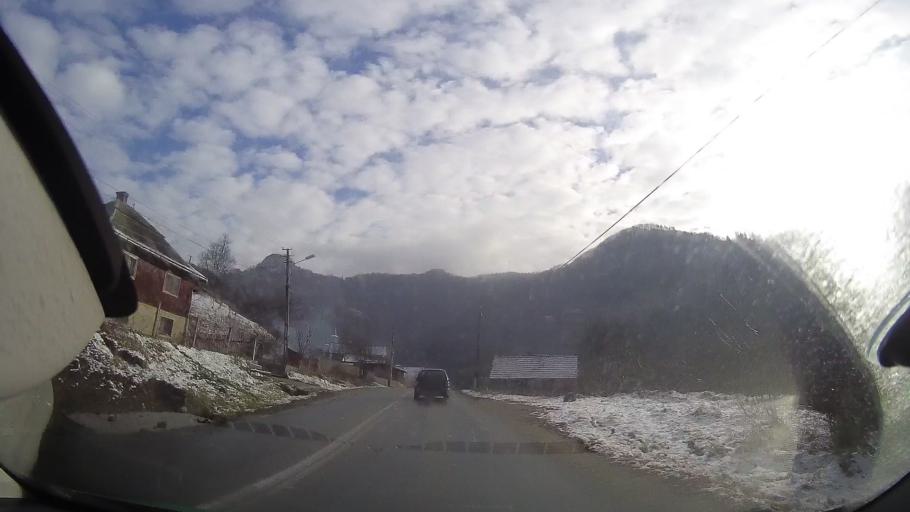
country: RO
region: Alba
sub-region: Oras Baia de Aries
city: Baia de Aries
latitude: 46.3905
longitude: 23.2911
